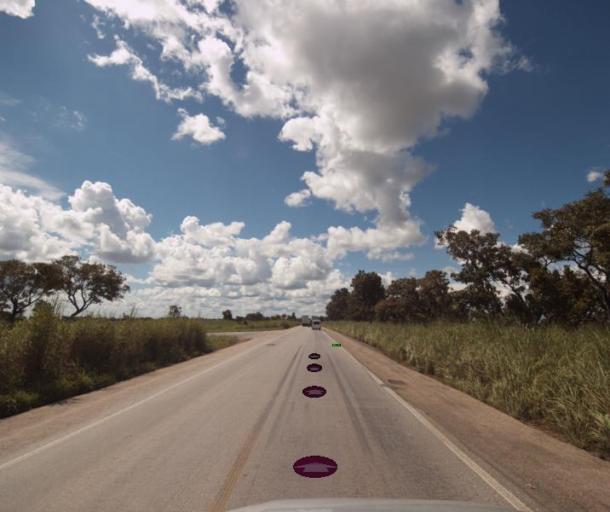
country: BR
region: Goias
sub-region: Porangatu
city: Porangatu
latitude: -13.6074
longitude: -49.0421
